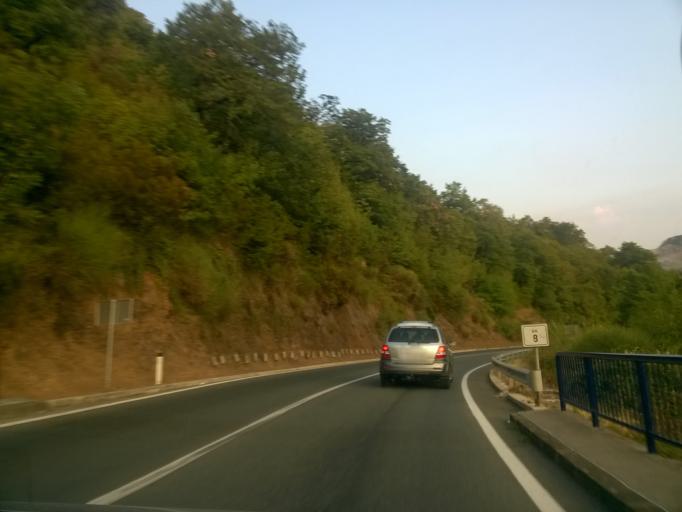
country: ME
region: Bar
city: Sutomore
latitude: 42.1730
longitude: 19.0079
